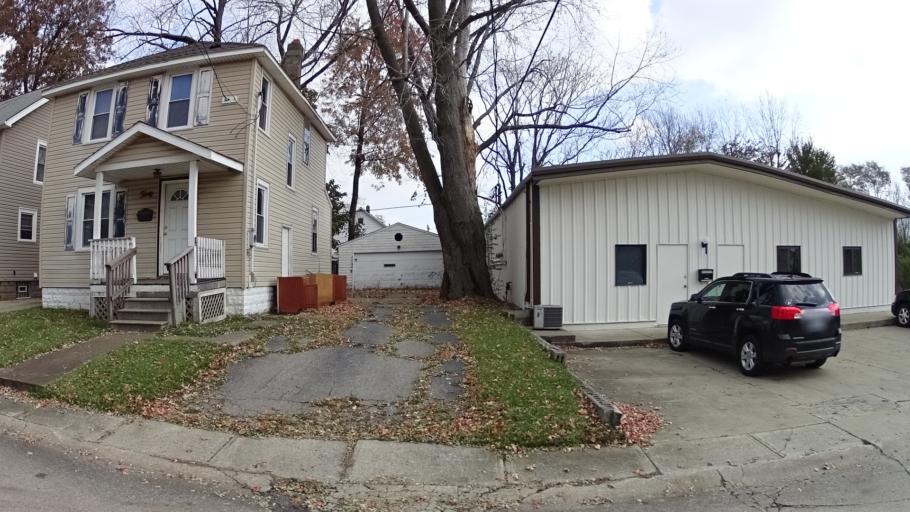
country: US
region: Ohio
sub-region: Lorain County
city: Elyria
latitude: 41.3725
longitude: -82.0910
